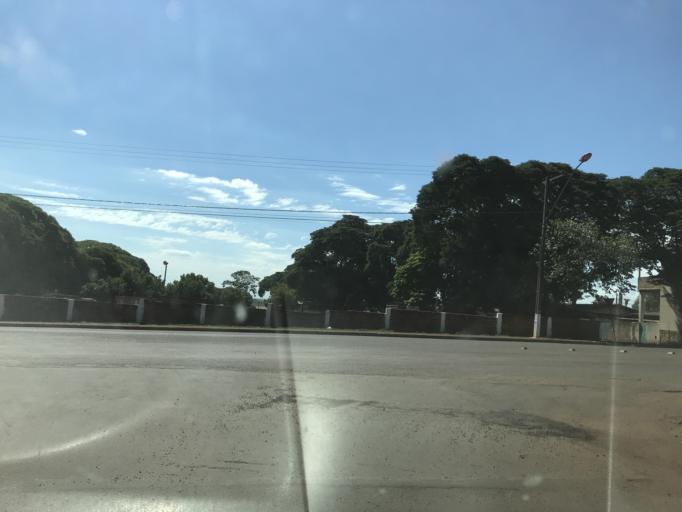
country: BR
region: Parana
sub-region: Palotina
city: Palotina
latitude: -24.2864
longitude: -53.8507
